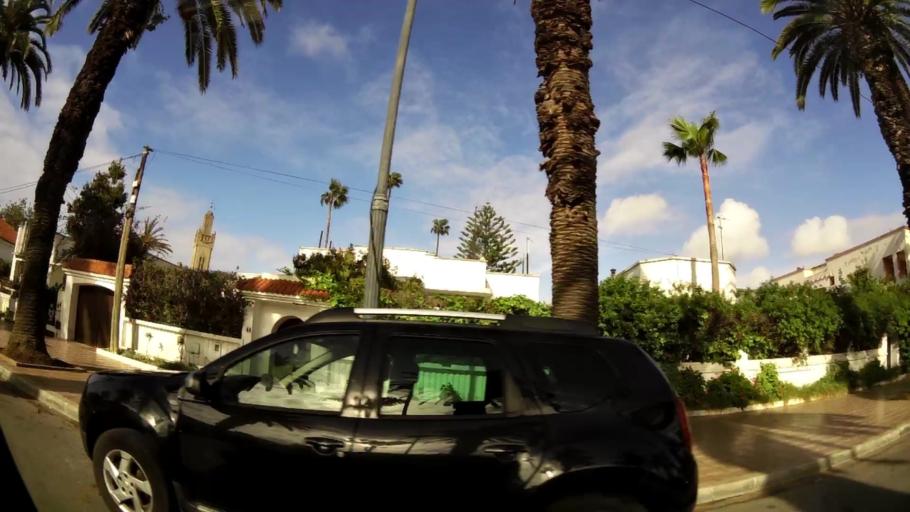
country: MA
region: Grand Casablanca
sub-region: Mohammedia
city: Mohammedia
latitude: 33.7002
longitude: -7.3933
